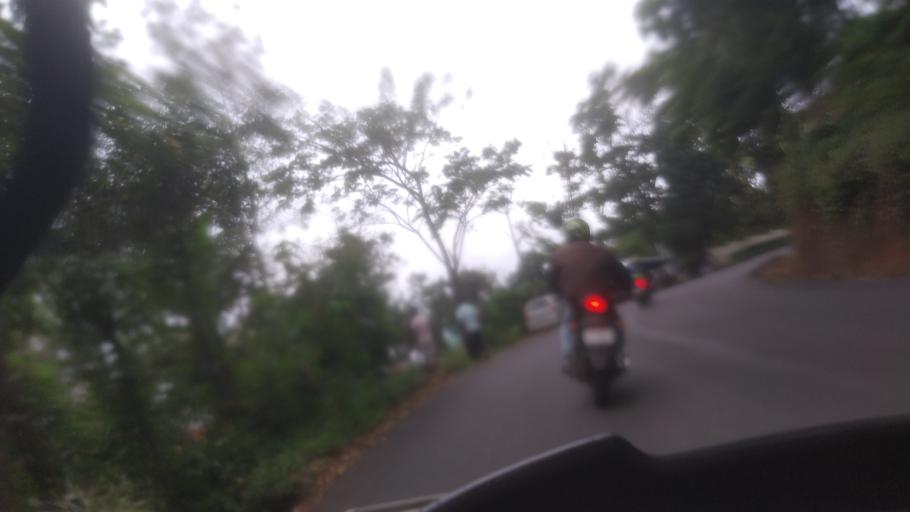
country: IN
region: Tamil Nadu
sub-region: Theni
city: Kombai
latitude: 9.8940
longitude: 77.1416
